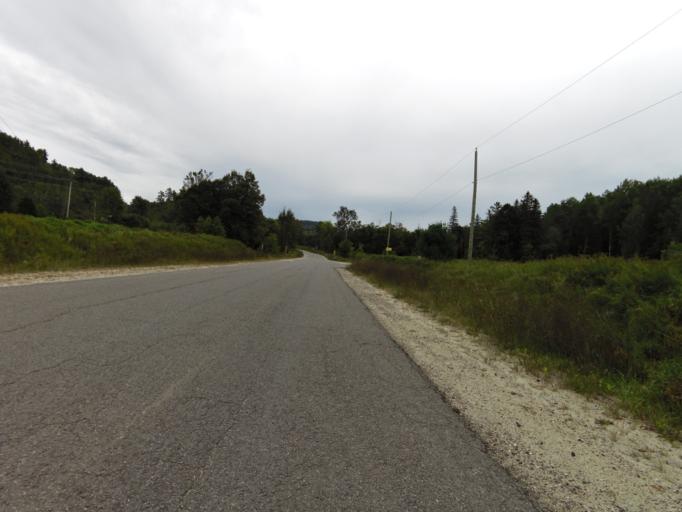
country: CA
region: Quebec
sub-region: Outaouais
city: Wakefield
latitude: 45.8100
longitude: -75.9409
